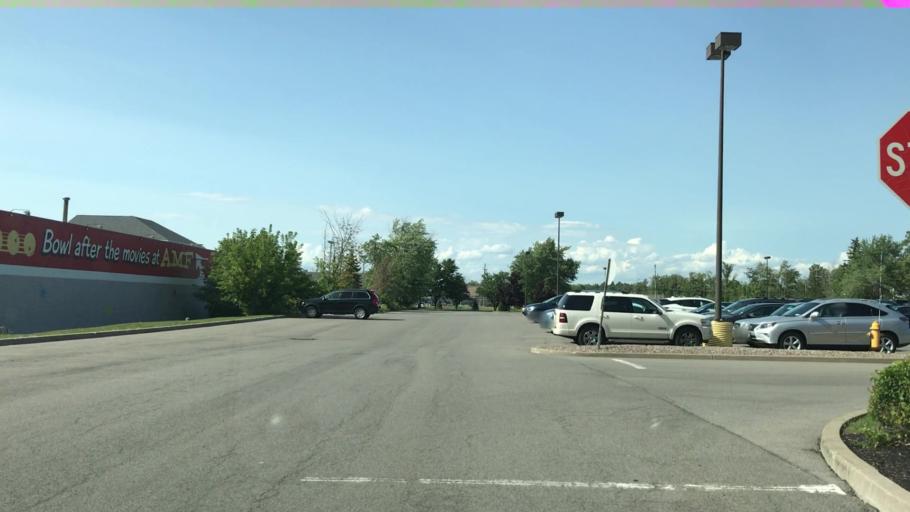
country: US
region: New York
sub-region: Erie County
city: Depew
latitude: 42.8783
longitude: -78.6945
